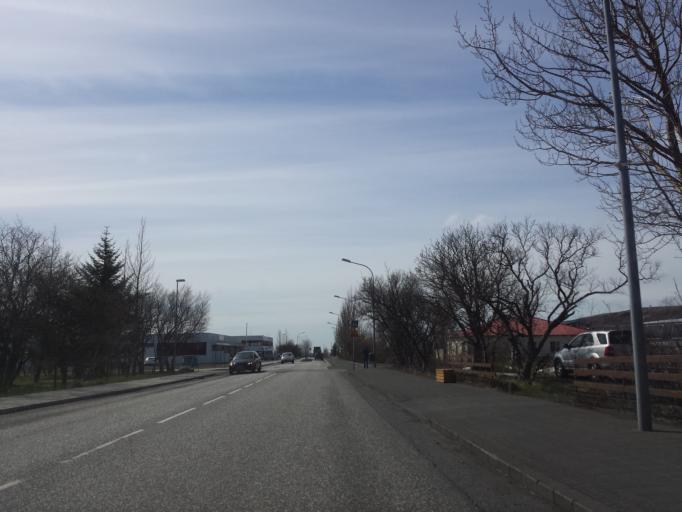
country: IS
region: South
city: Hveragerdi
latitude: 63.9989
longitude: -21.1880
